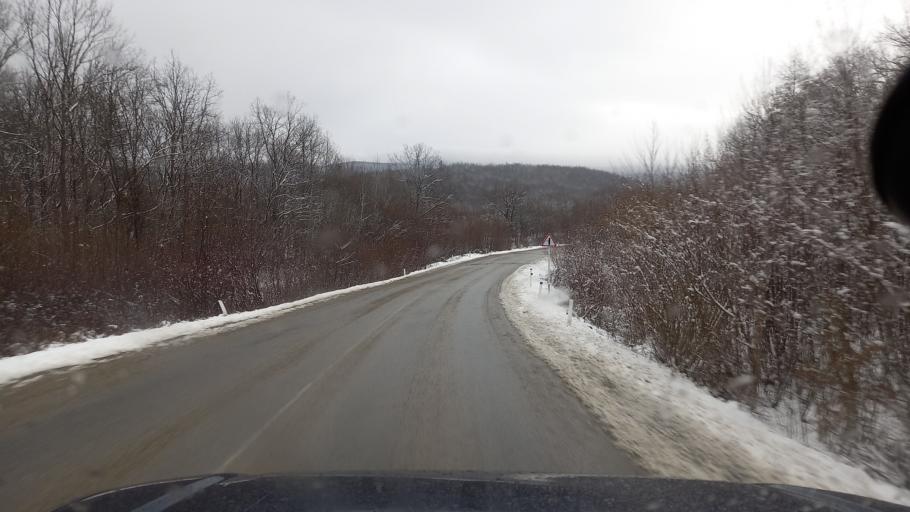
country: RU
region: Adygeya
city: Abadzekhskaya
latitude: 44.3805
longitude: 40.2477
